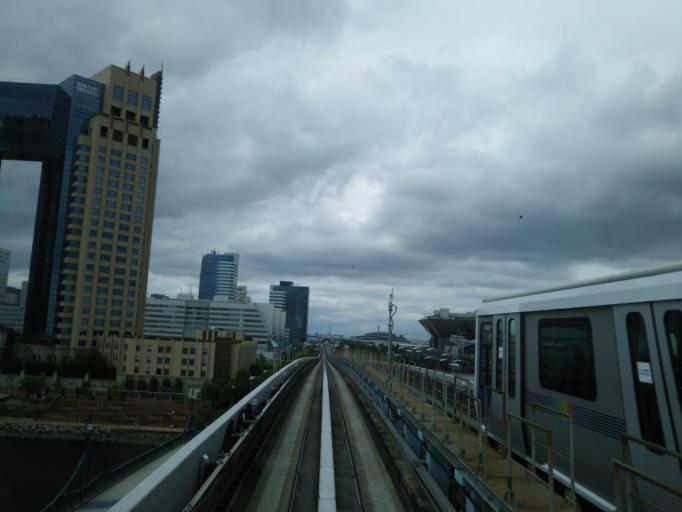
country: JP
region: Tokyo
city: Urayasu
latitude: 35.6271
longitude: 139.7856
